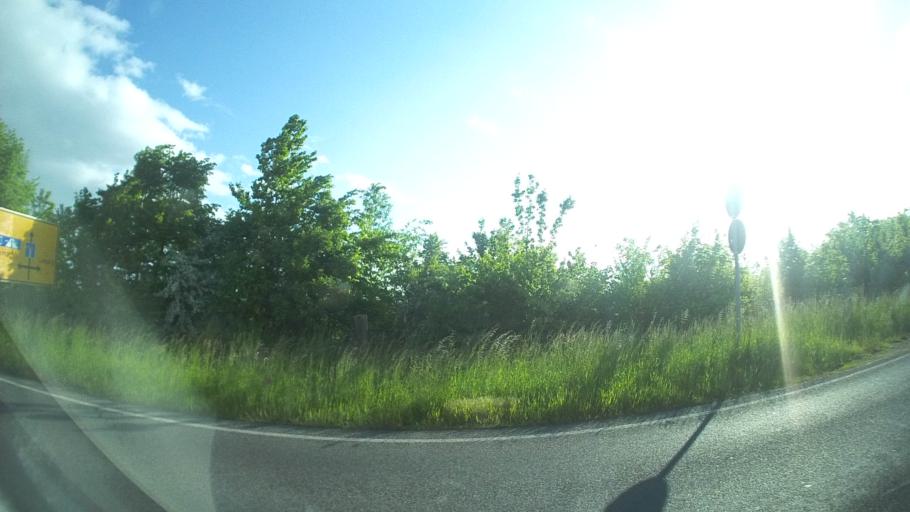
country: DE
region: Saxony
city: Grossposna
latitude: 51.2867
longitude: 12.4519
